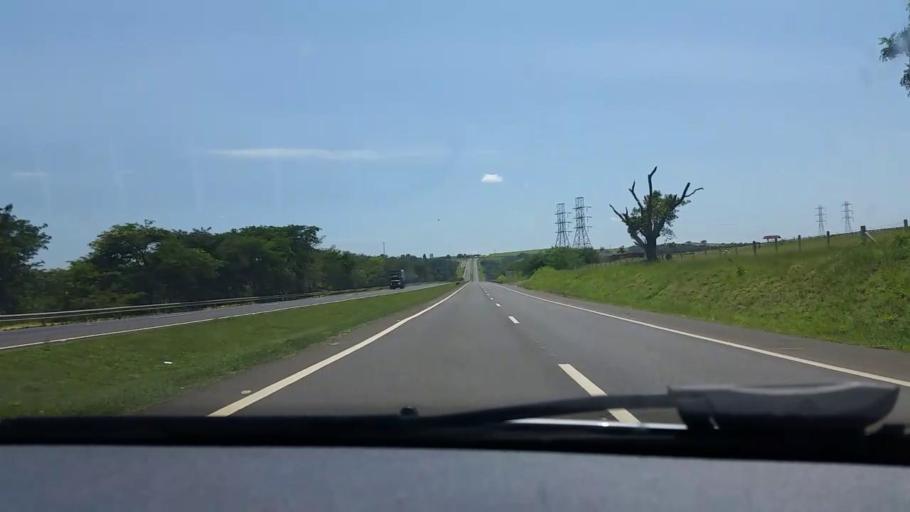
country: BR
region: Sao Paulo
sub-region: Bauru
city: Bauru
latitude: -22.4132
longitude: -49.1049
